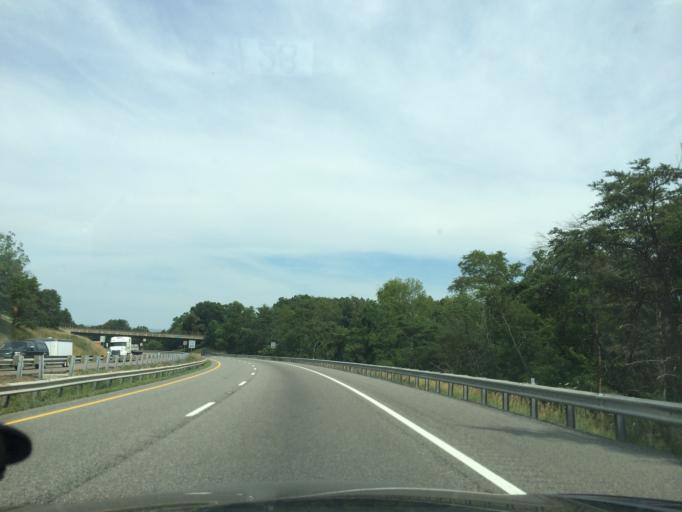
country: US
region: West Virginia
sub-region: Morgan County
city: Berkeley Springs
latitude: 39.6643
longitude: -78.4246
